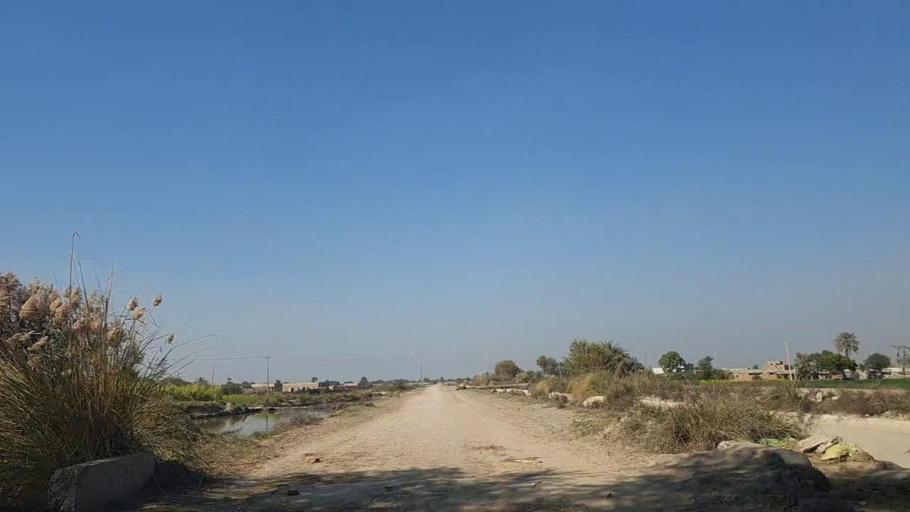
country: PK
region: Sindh
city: Sakrand
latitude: 26.2732
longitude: 68.2199
